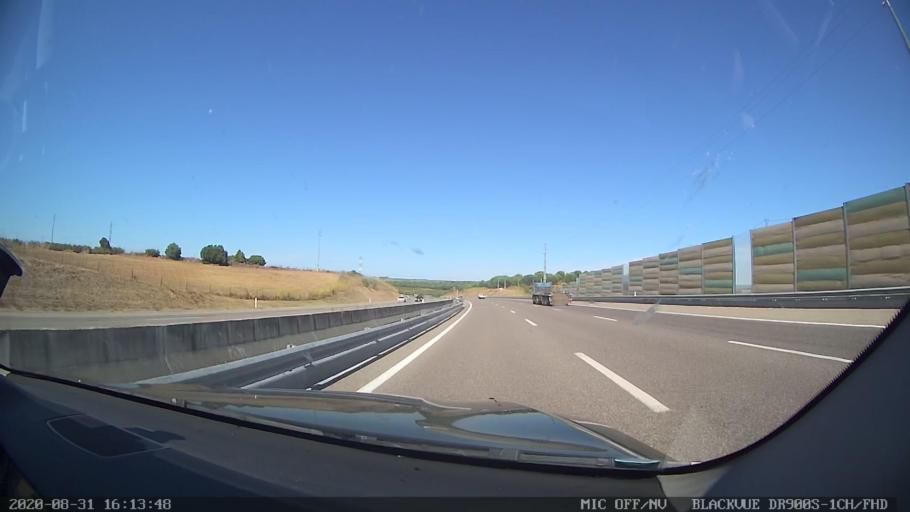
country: PT
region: Santarem
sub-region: Santarem
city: Santarem
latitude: 39.2793
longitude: -8.6986
